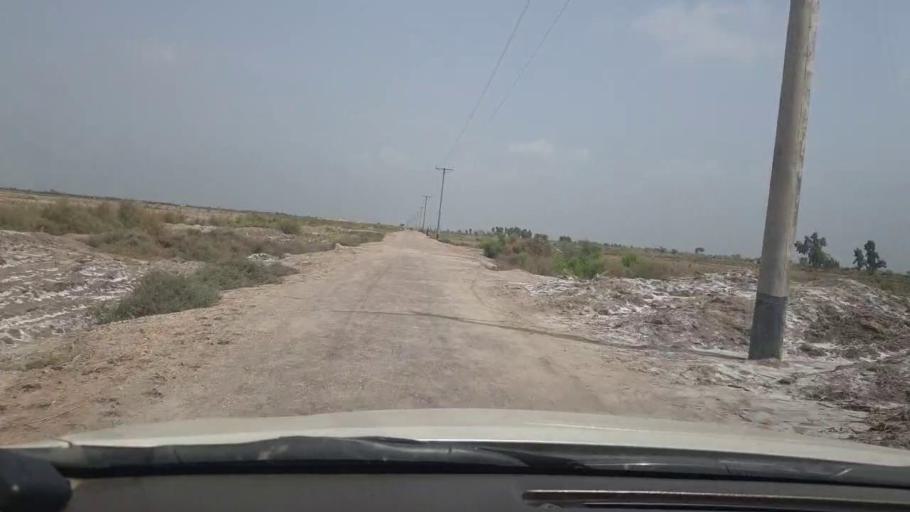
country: PK
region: Sindh
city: Garhi Yasin
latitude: 27.9953
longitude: 68.5010
